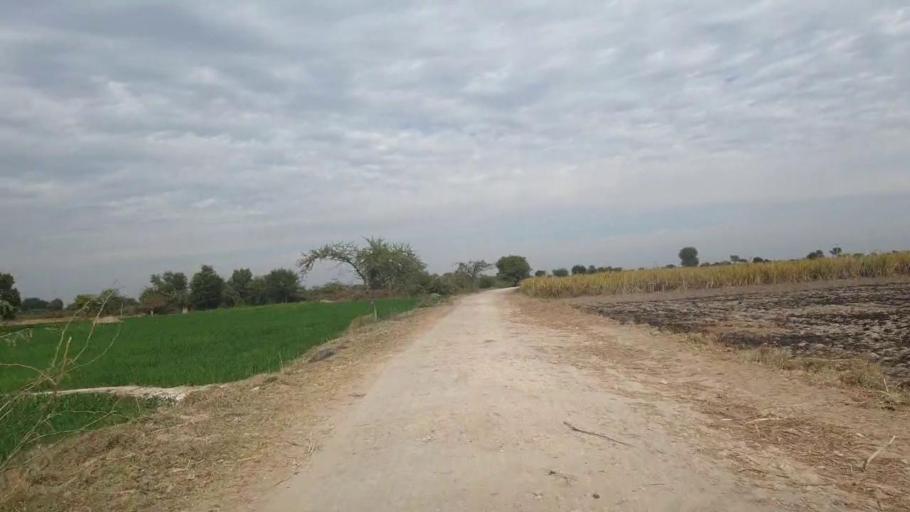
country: PK
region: Sindh
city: Jhol
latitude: 26.0128
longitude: 68.8726
